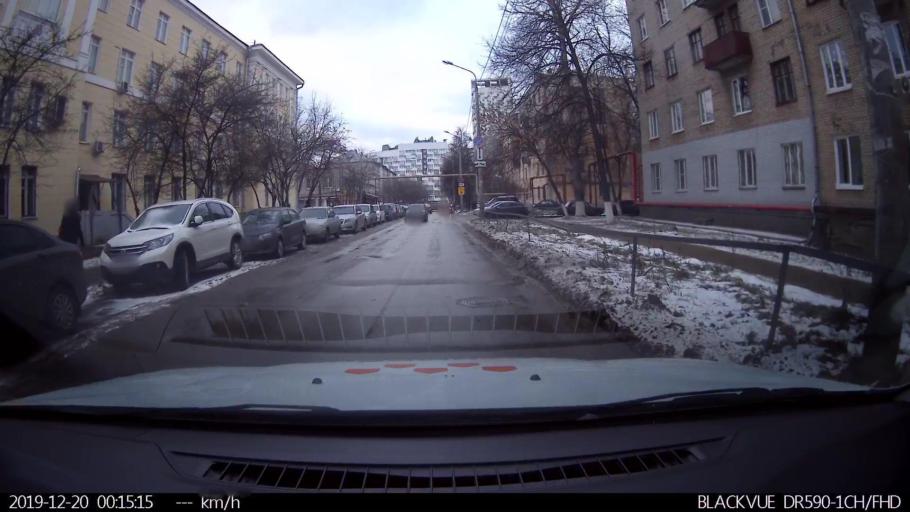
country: RU
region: Jaroslavl
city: Porech'ye-Rybnoye
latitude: 56.9967
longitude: 39.3860
